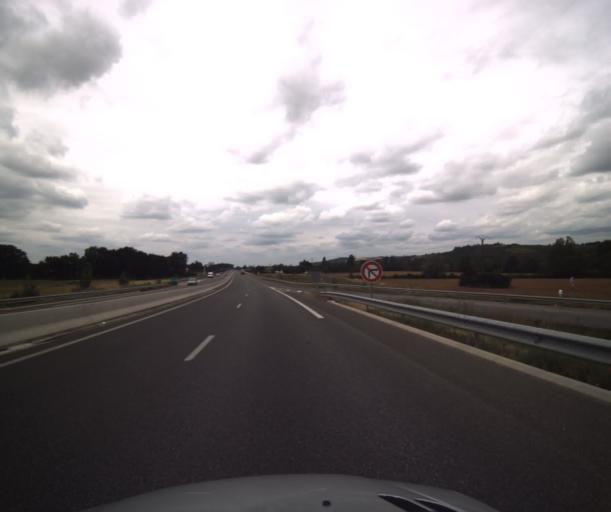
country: FR
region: Midi-Pyrenees
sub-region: Departement de la Haute-Garonne
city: Vernet
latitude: 43.4487
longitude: 1.4198
